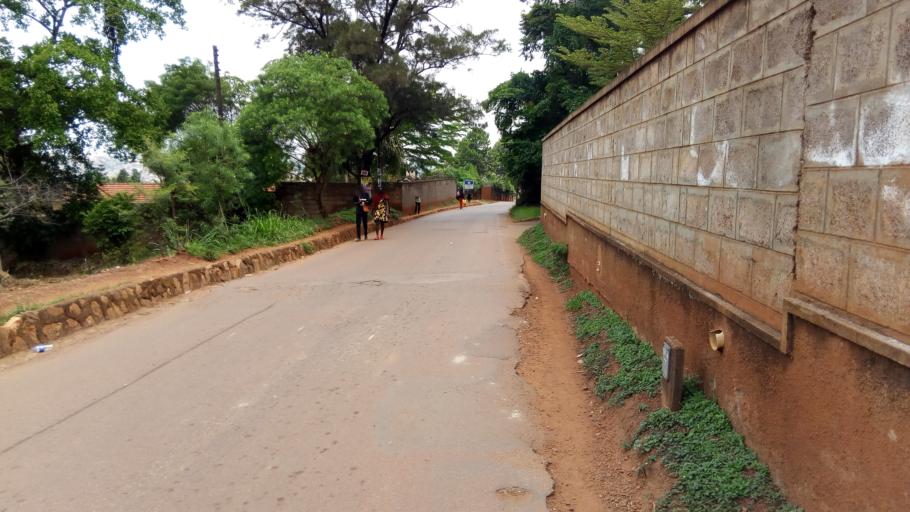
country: UG
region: Central Region
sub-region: Wakiso District
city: Kireka
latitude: 0.3217
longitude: 32.6267
